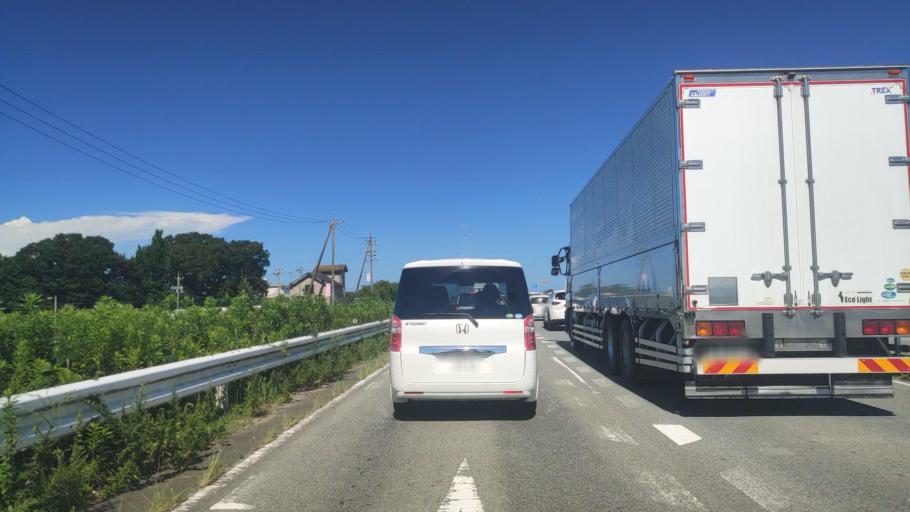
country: JP
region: Mie
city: Ise
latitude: 34.5874
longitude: 136.5933
